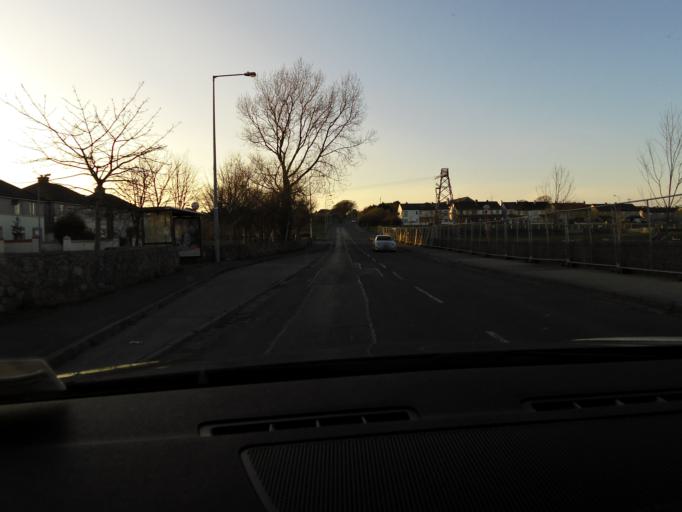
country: IE
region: Connaught
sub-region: County Galway
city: Gaillimh
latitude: 53.2750
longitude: -9.0819
